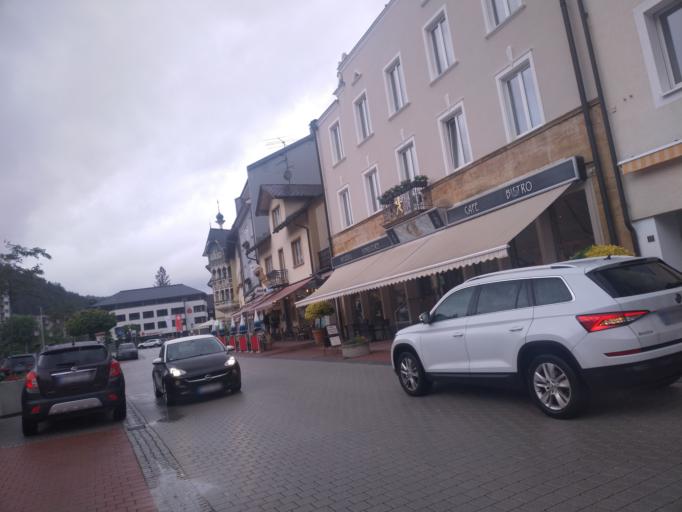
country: DE
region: Baden-Wuerttemberg
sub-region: Freiburg Region
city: Sankt Blasien
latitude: 47.7614
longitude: 8.1297
